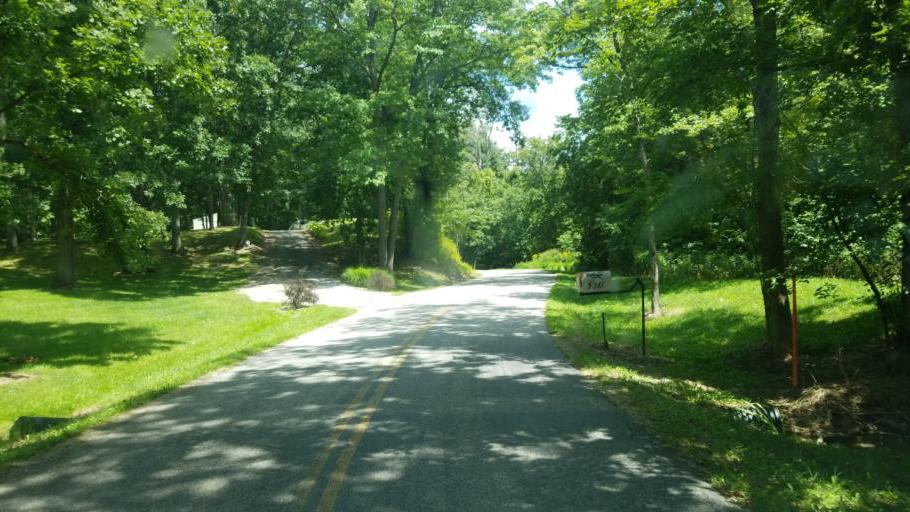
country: US
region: Ohio
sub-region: Delaware County
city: Sunbury
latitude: 40.2973
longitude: -82.8257
